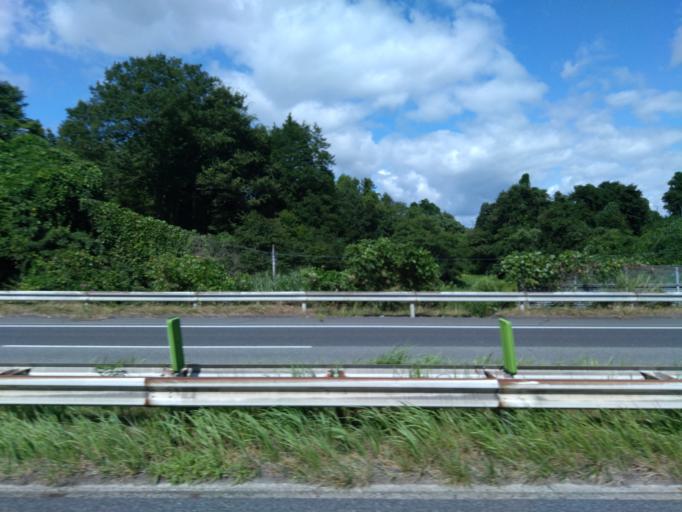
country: JP
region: Miyagi
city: Kogota
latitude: 38.7352
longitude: 141.0434
